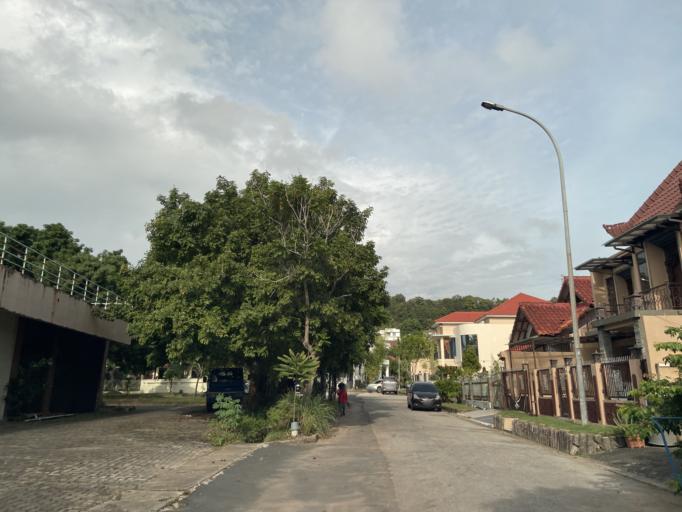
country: SG
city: Singapore
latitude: 1.1124
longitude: 104.0235
